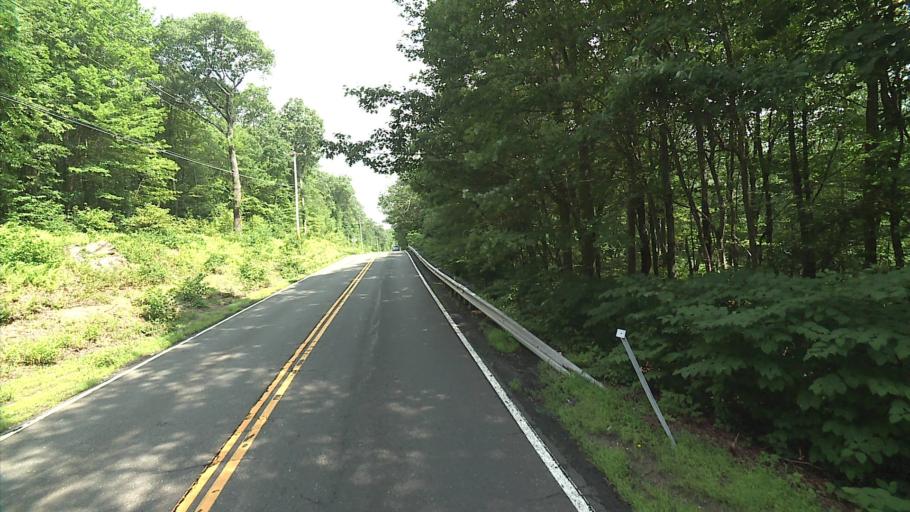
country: US
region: Connecticut
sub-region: New Haven County
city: Wolcott
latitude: 41.5783
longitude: -72.9513
